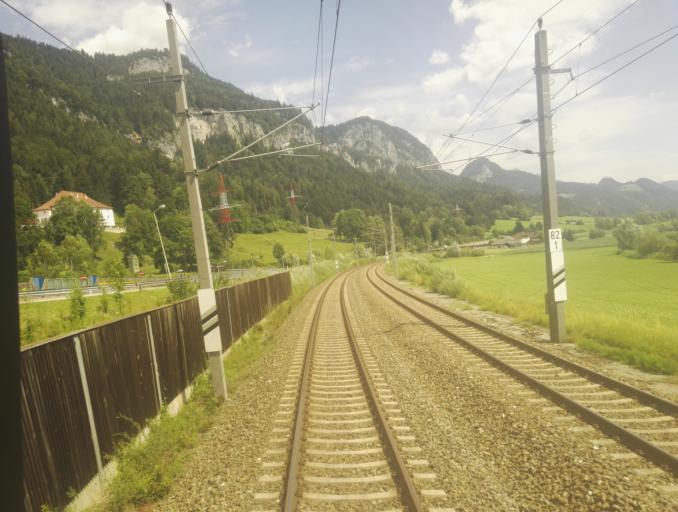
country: AT
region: Styria
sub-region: Politischer Bezirk Liezen
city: Stainach
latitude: 47.5399
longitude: 14.1196
